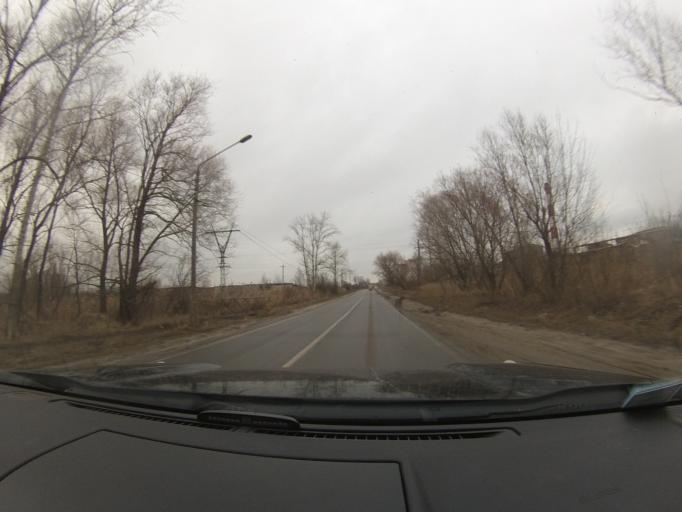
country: RU
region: Moskovskaya
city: Lopatinskiy
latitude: 55.3421
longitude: 38.7314
